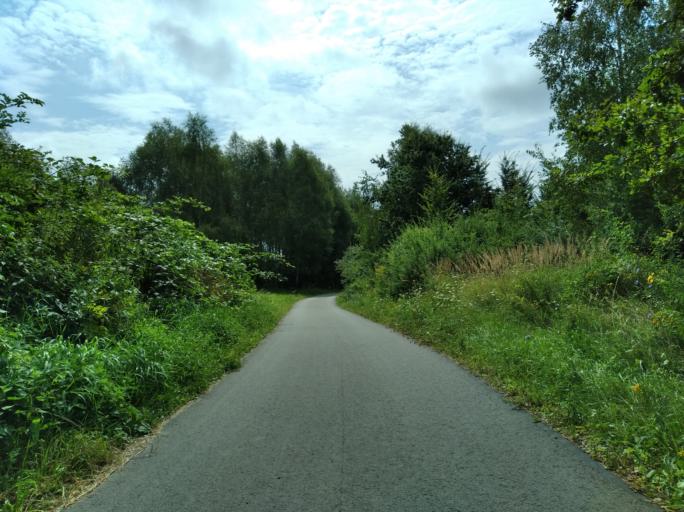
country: PL
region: Subcarpathian Voivodeship
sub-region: Powiat krosnienski
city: Leki
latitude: 49.8129
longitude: 21.6660
